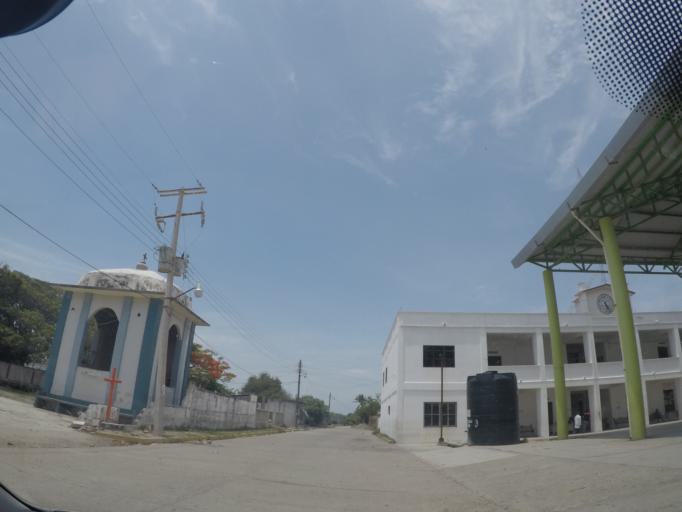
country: MX
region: Oaxaca
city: San Mateo del Mar
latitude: 16.2103
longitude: -94.9821
